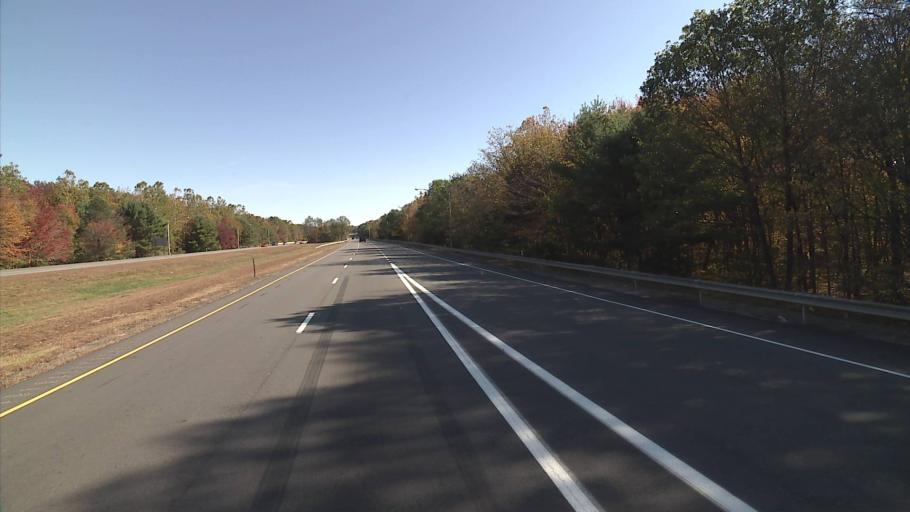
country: US
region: Connecticut
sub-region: Windham County
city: Willimantic
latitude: 41.7318
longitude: -72.1967
